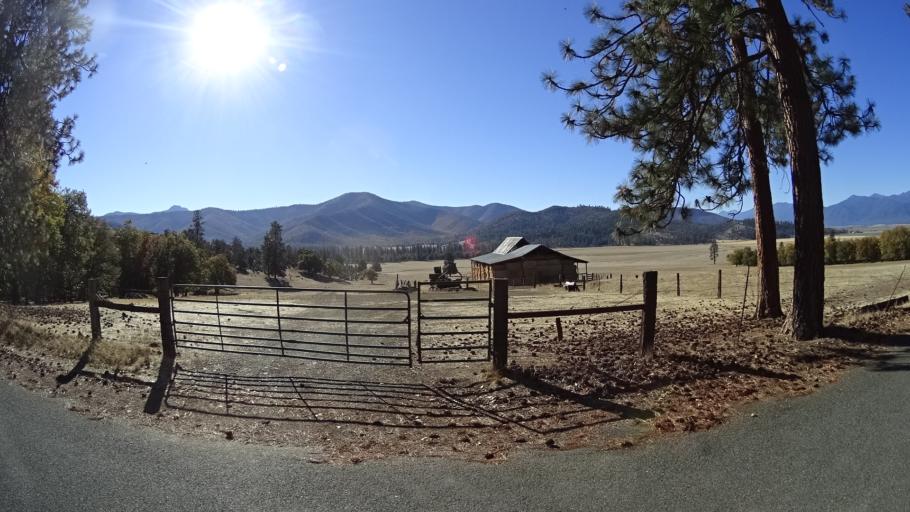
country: US
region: California
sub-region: Siskiyou County
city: Yreka
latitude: 41.5783
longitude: -122.8033
